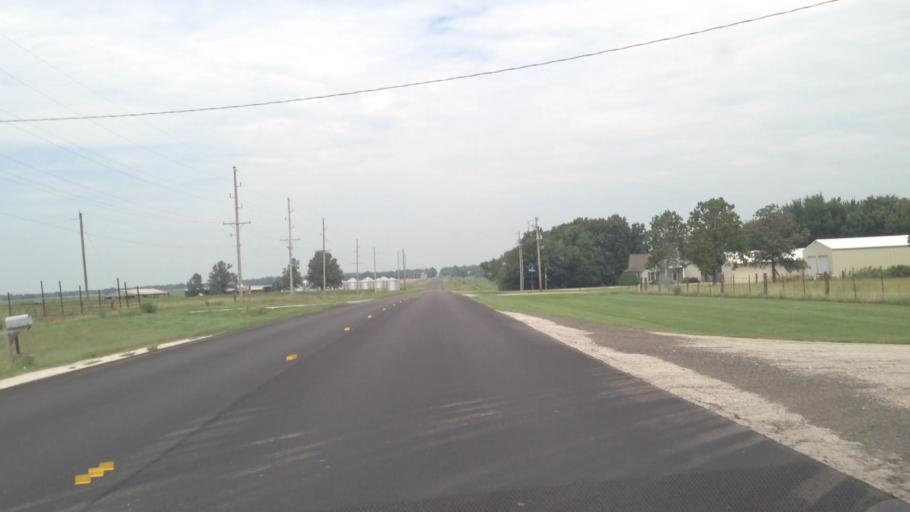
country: US
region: Kansas
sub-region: Allen County
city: Iola
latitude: 37.8918
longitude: -95.1706
